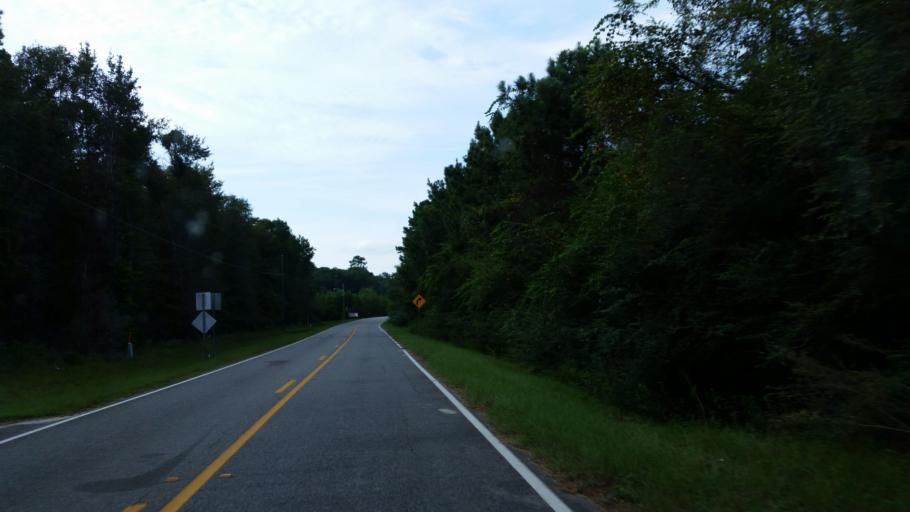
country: US
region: Georgia
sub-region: Lowndes County
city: Hahira
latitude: 31.0065
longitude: -83.3877
